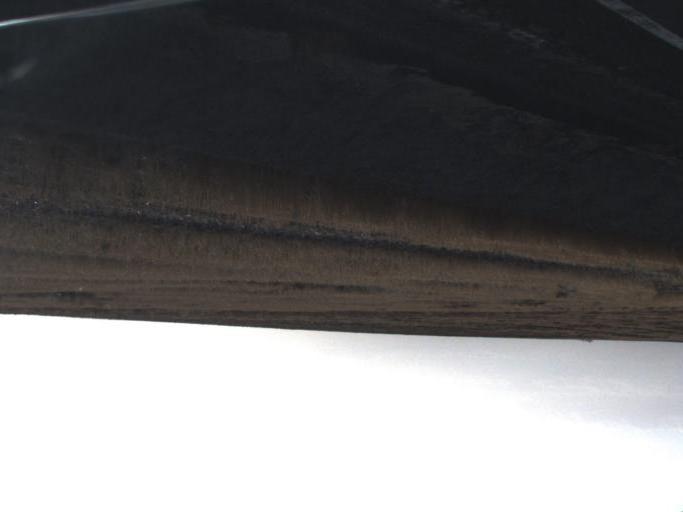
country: US
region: Washington
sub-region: Adams County
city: Ritzville
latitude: 47.2539
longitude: -118.6859
